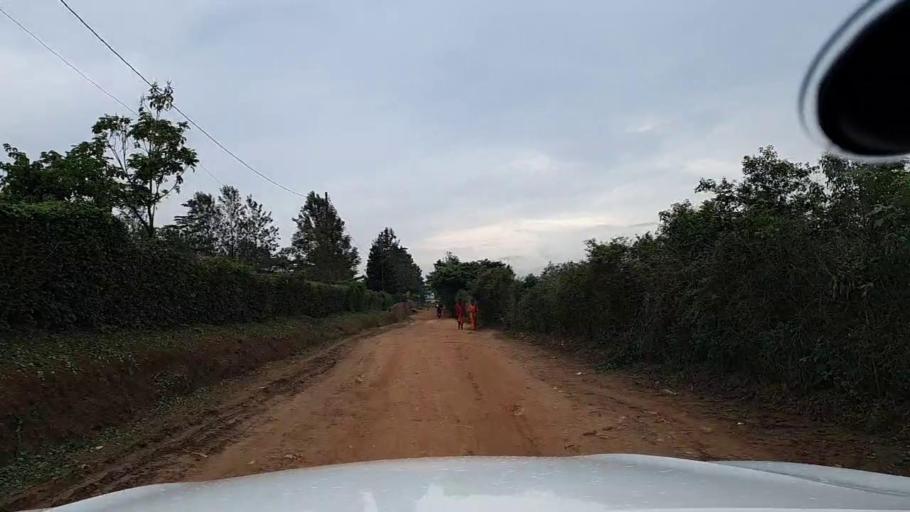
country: RW
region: Kigali
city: Kigali
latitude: -1.9603
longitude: 29.9965
